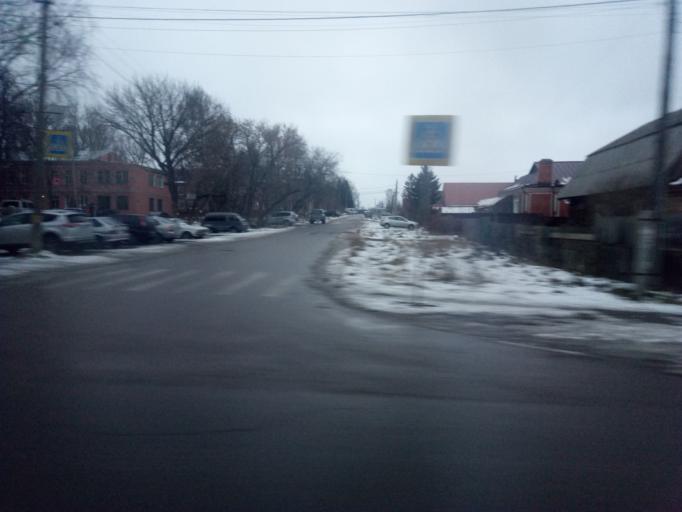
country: RU
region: Tula
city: Tula
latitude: 54.1985
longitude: 37.5603
